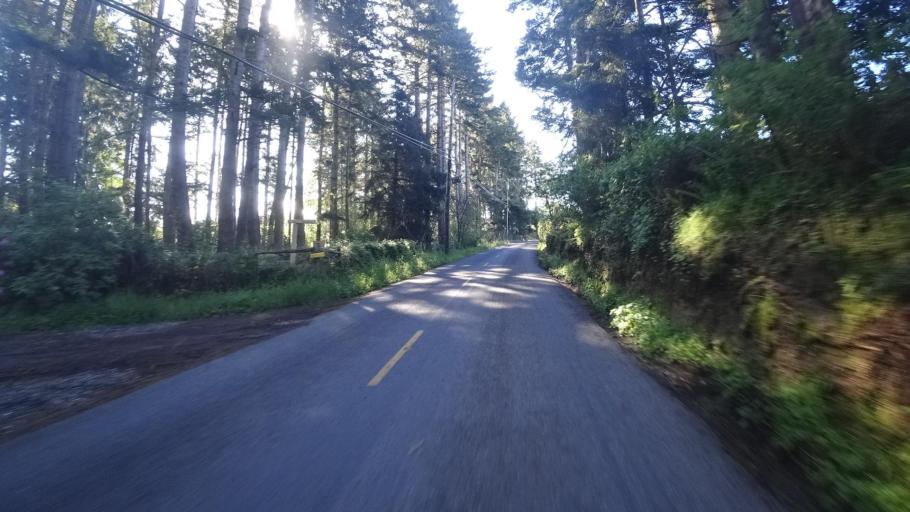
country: US
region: California
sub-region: Humboldt County
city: McKinleyville
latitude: 40.9807
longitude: -124.0970
